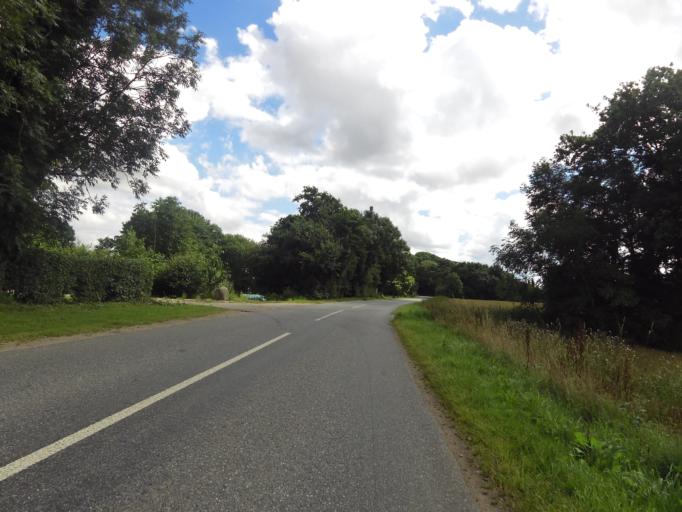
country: DK
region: South Denmark
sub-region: Haderslev Kommune
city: Vojens
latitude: 55.2817
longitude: 9.2421
